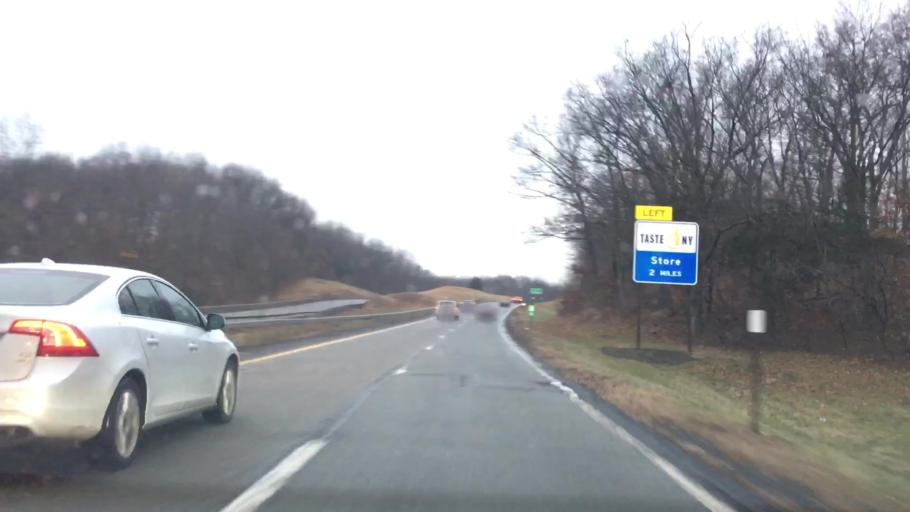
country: US
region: New York
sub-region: Dutchess County
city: Hillside Lake
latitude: 41.6272
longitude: -73.7775
